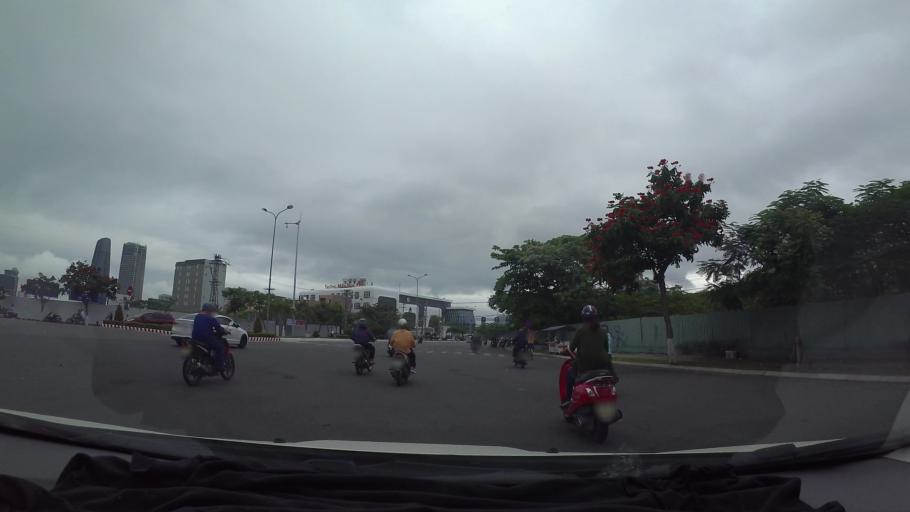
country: VN
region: Da Nang
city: Da Nang
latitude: 16.0732
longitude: 108.2308
